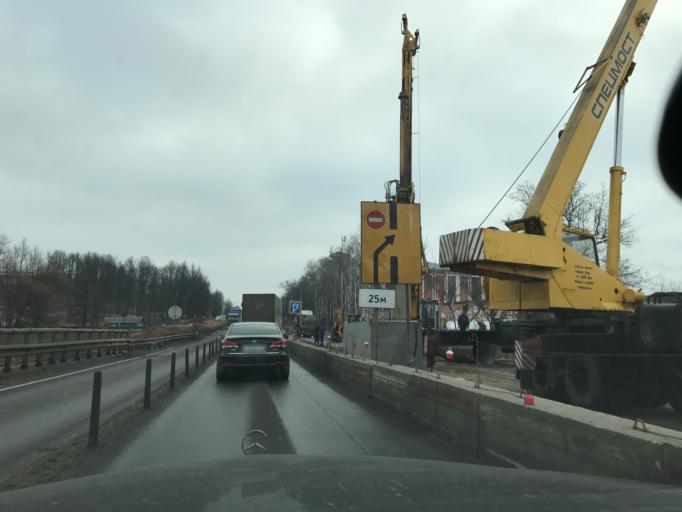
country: RU
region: Vladimir
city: Lakinsk
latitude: 56.0114
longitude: 39.9416
